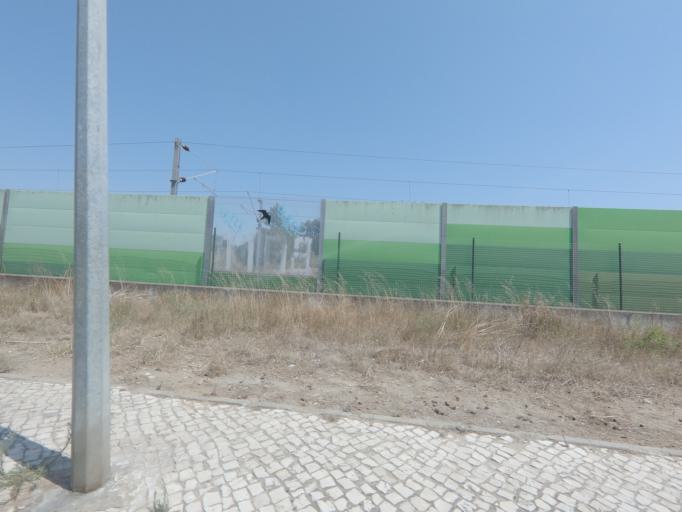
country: PT
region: Setubal
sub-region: Setubal
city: Setubal
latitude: 38.5428
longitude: -8.8826
